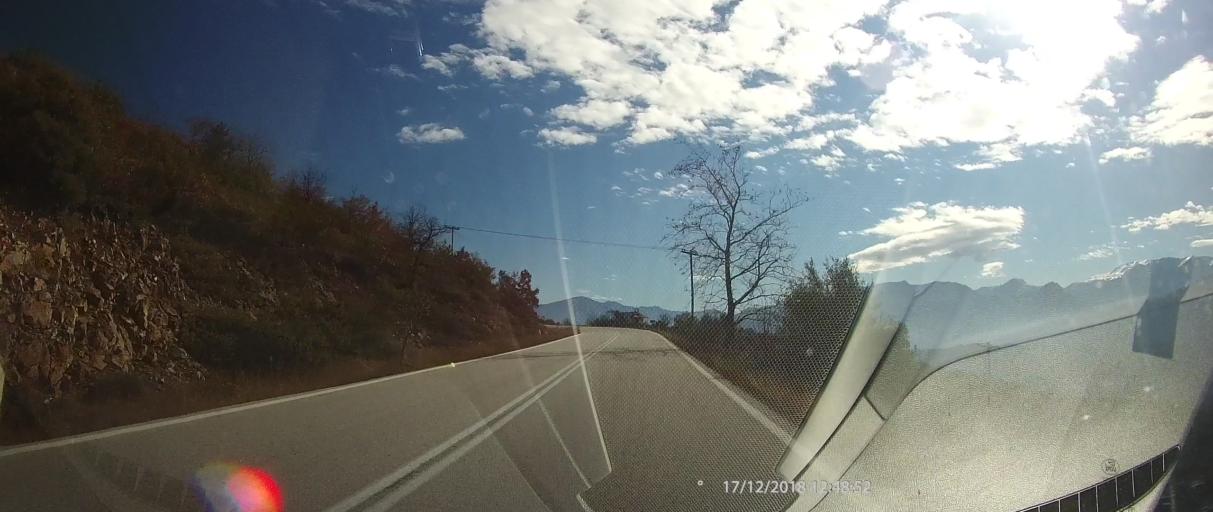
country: GR
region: Thessaly
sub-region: Trikala
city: Kastraki
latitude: 39.7822
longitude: 21.4392
